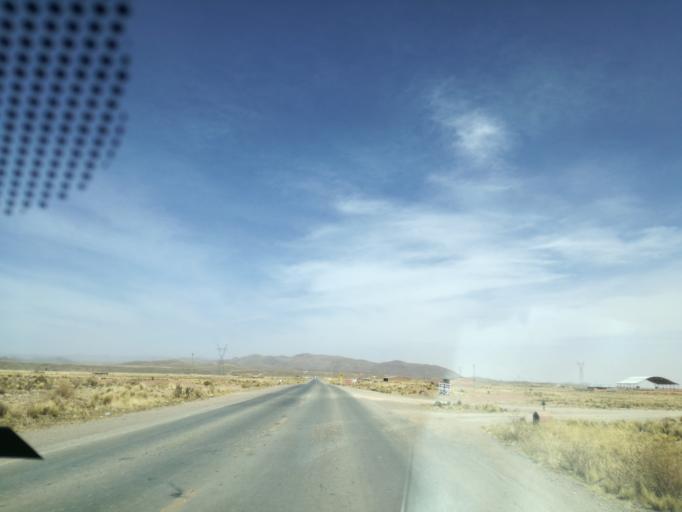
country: BO
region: Oruro
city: Oruro
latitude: -17.7999
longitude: -67.0235
